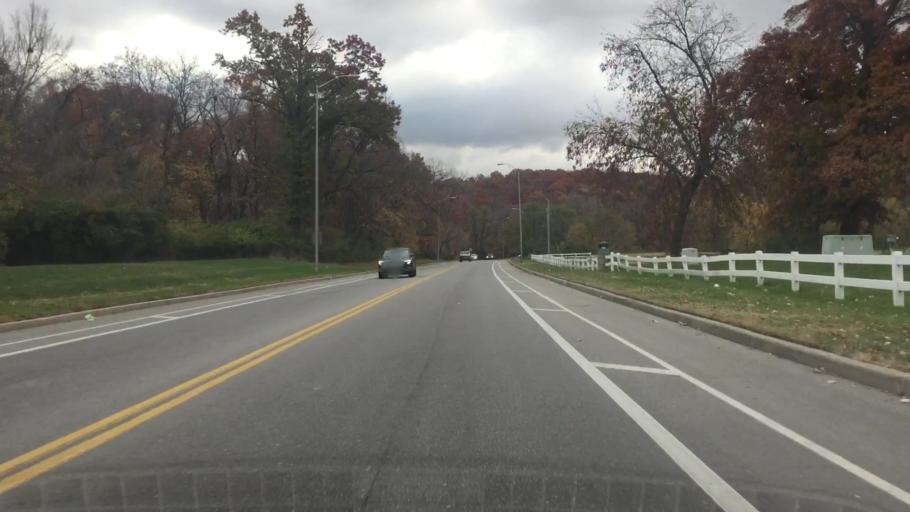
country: US
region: Missouri
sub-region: Jackson County
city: Raytown
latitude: 38.9961
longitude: -94.5256
